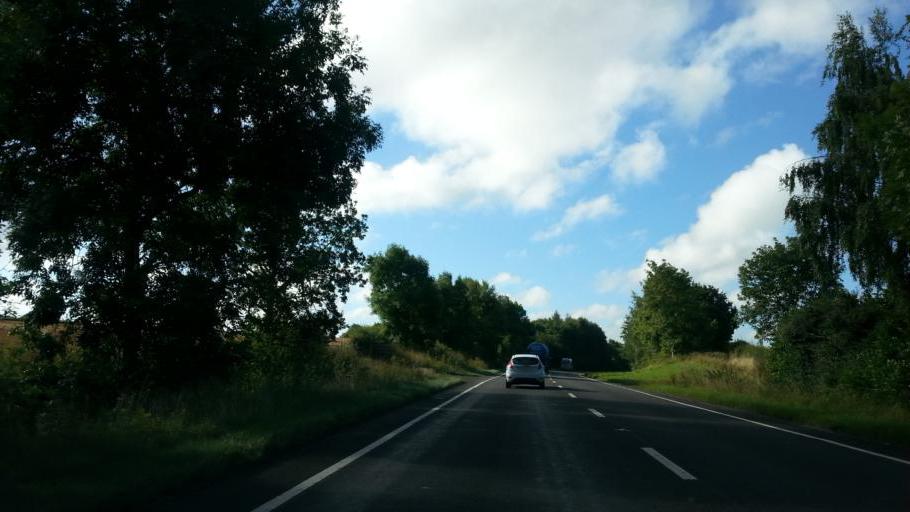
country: GB
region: England
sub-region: District of Rutland
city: South Luffenham
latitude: 52.5296
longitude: -0.5894
